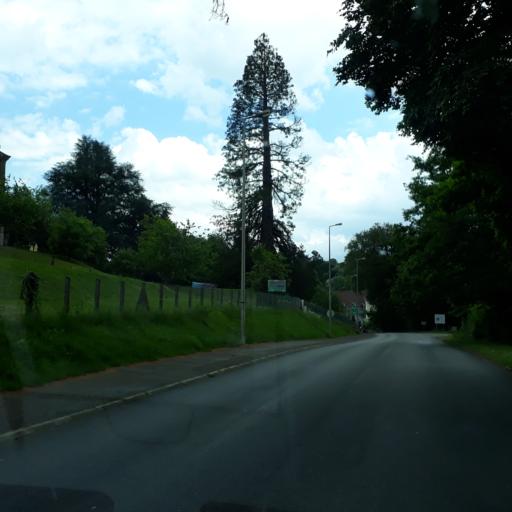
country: FR
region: Limousin
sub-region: Departement de la Haute-Vienne
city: Eymoutiers
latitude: 45.7407
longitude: 1.7368
